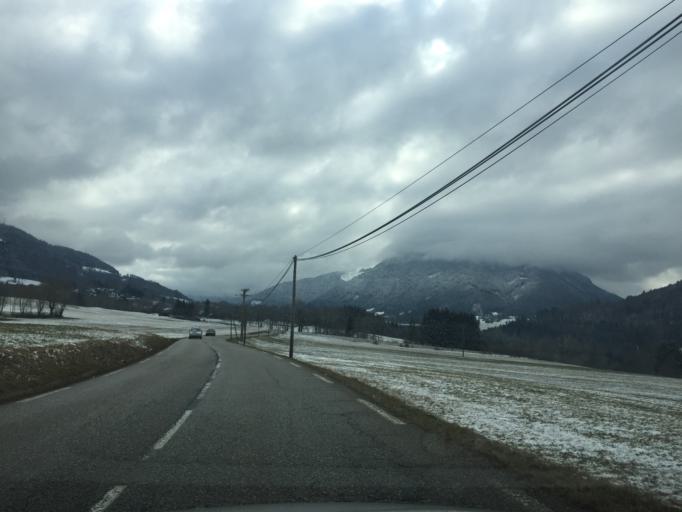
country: FR
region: Rhone-Alpes
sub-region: Departement de la Haute-Savoie
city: Gruffy
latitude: 45.7104
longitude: 6.1148
